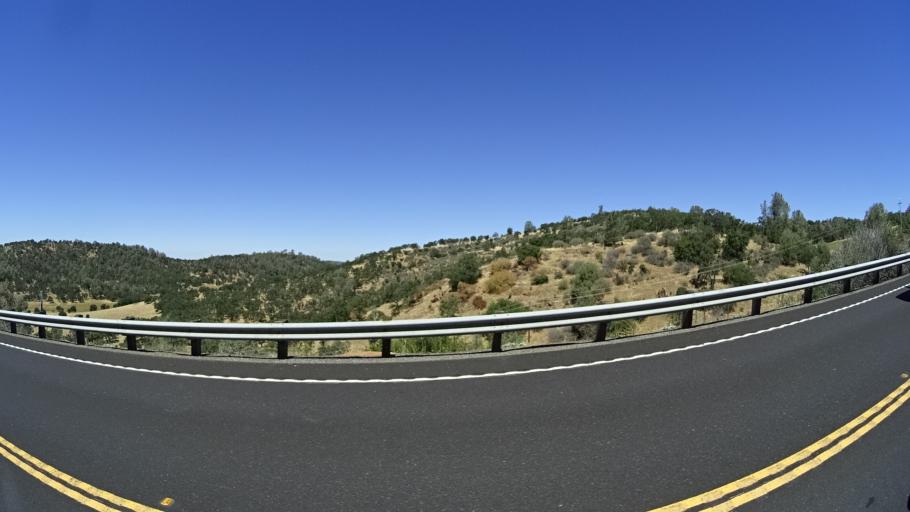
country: US
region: California
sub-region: Calaveras County
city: Copperopolis
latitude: 38.0001
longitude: -120.6509
